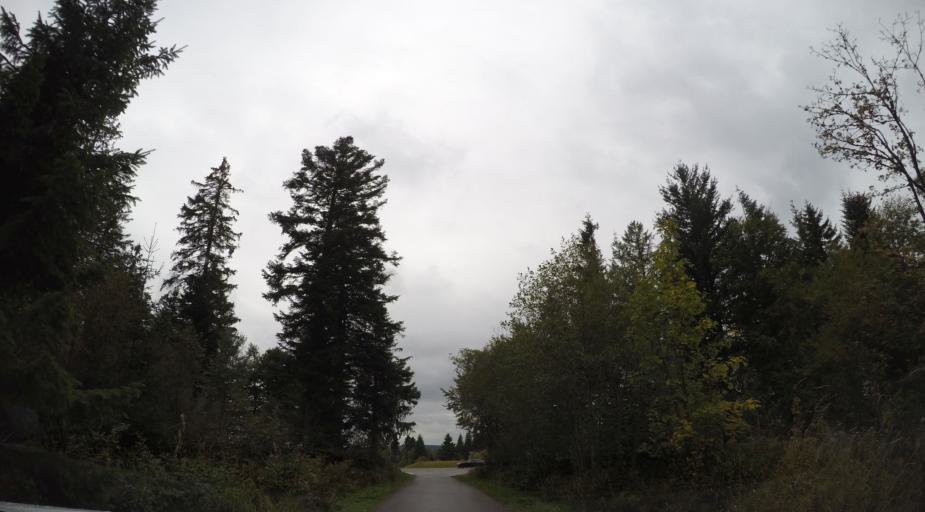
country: DE
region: Baden-Wuerttemberg
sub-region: Karlsruhe Region
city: Bad Rippoldsau-Schapbach
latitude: 48.4767
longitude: 8.2956
